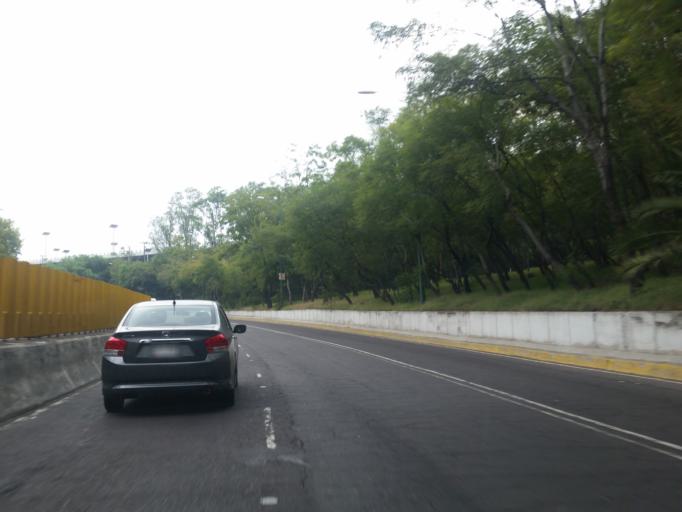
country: MX
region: Mexico City
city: Polanco
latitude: 19.4183
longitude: -99.1939
